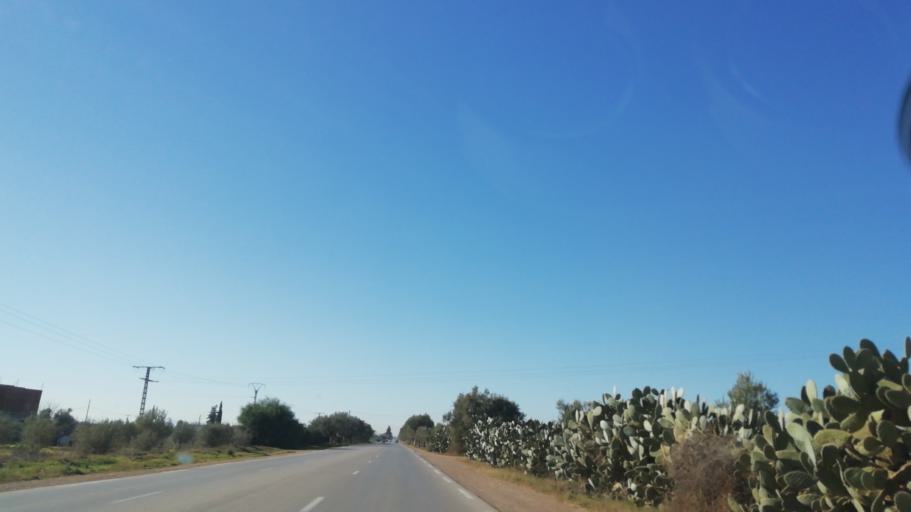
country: MA
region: Oriental
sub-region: Oujda-Angad
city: Oujda
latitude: 34.8285
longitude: -1.7917
